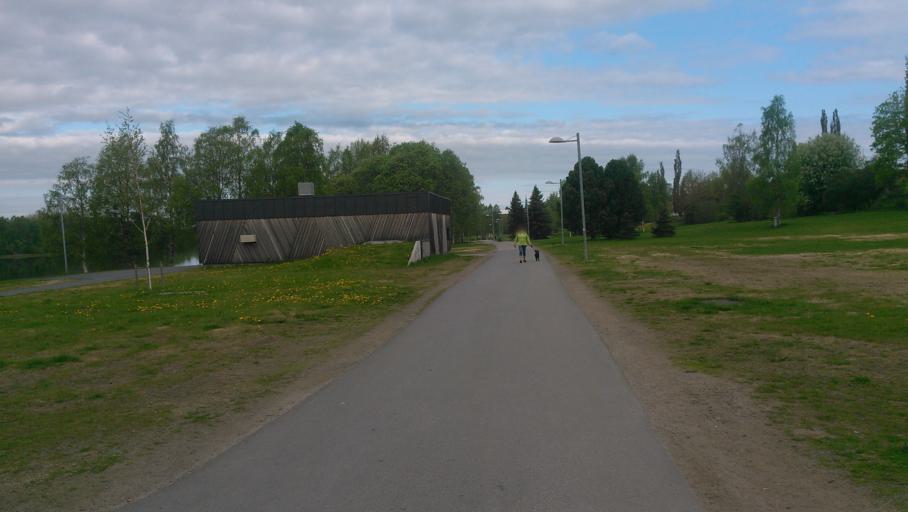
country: SE
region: Vaesterbotten
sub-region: Umea Kommun
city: Umea
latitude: 63.8168
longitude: 20.2893
